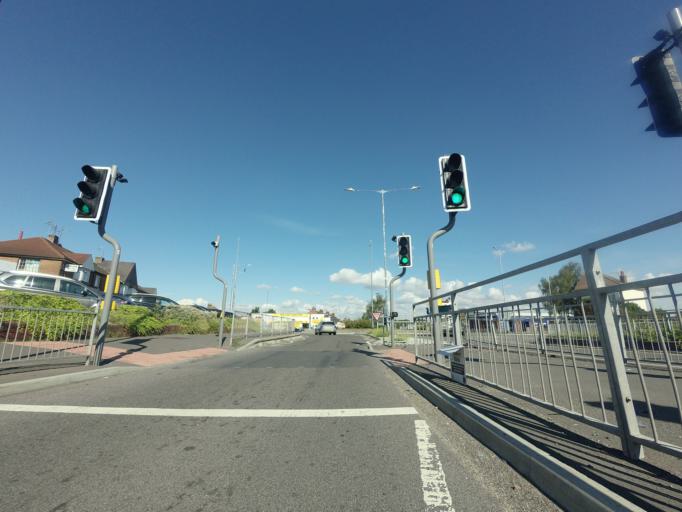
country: GB
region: England
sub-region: Kent
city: Gravesend
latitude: 51.4321
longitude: 0.3943
